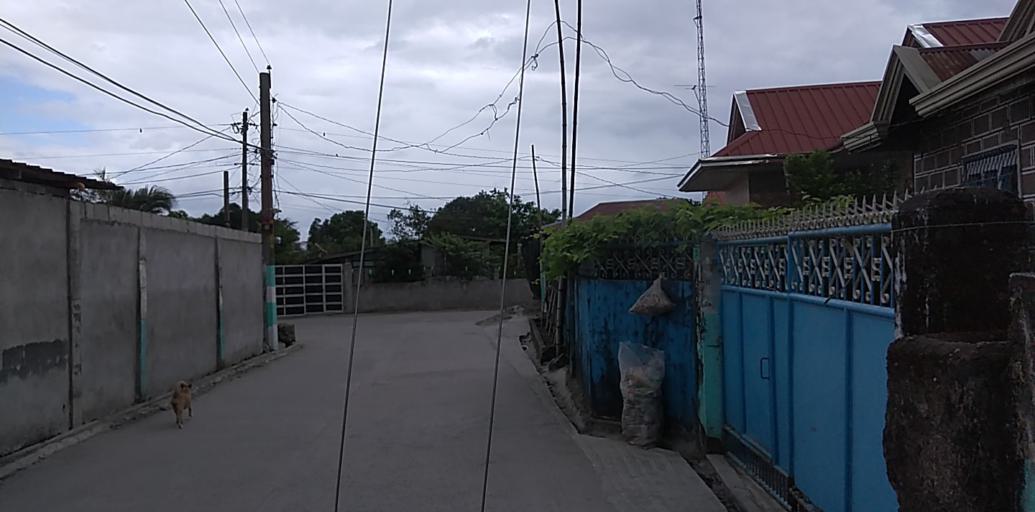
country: PH
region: Central Luzon
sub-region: Province of Pampanga
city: Pio
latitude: 15.0444
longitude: 120.5372
